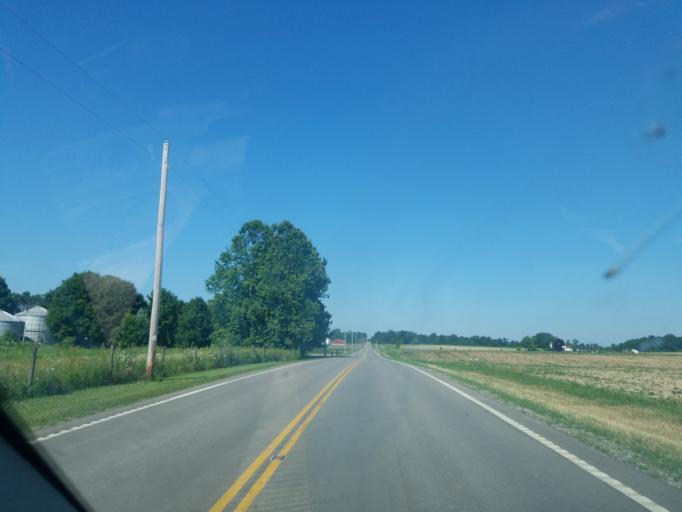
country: US
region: Ohio
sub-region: Logan County
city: Northwood
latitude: 40.4535
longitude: -83.7419
